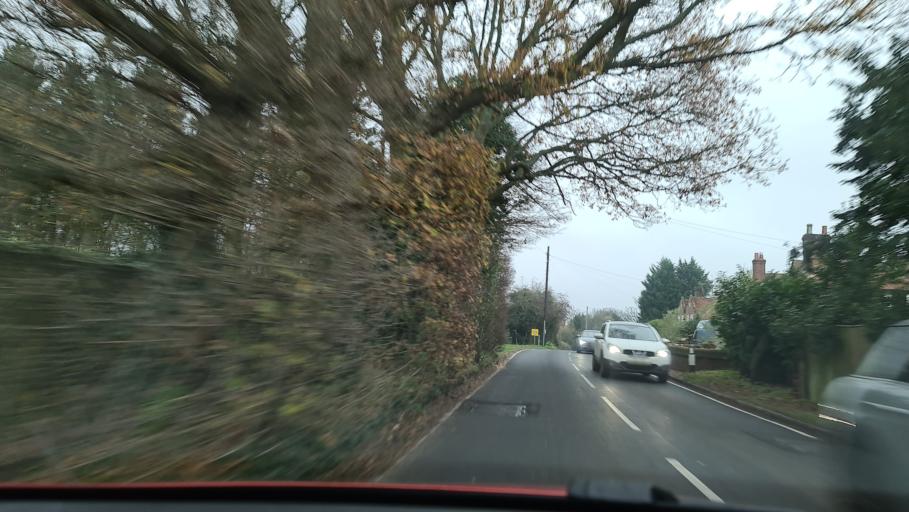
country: GB
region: England
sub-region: Buckinghamshire
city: Beaconsfield
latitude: 51.6317
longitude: -0.6830
